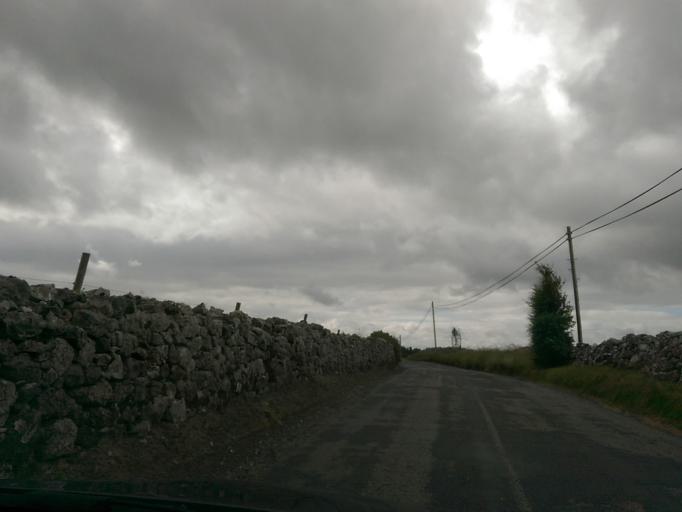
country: IE
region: Connaught
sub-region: County Galway
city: Loughrea
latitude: 53.2277
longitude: -8.5592
